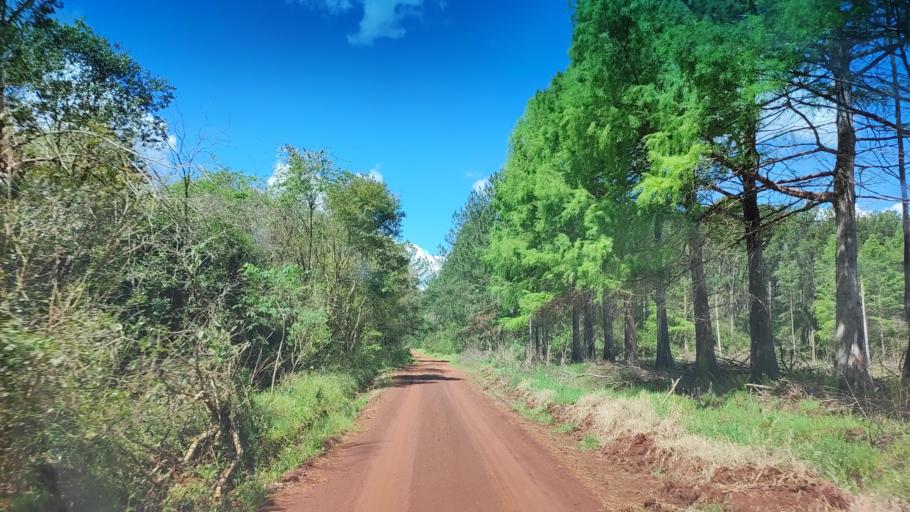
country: AR
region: Misiones
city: Ruiz de Montoya
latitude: -26.9529
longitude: -55.0355
